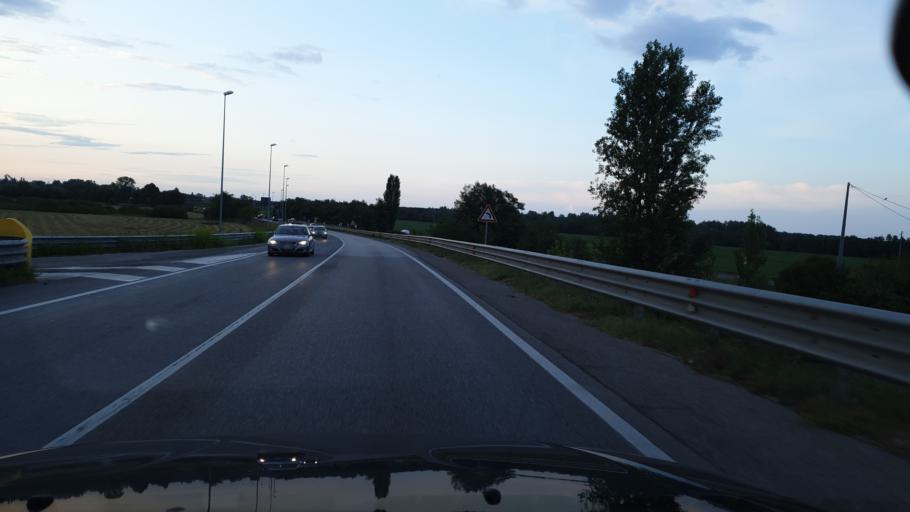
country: IT
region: Emilia-Romagna
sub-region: Provincia di Ravenna
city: Savio
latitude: 44.3177
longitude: 12.2842
